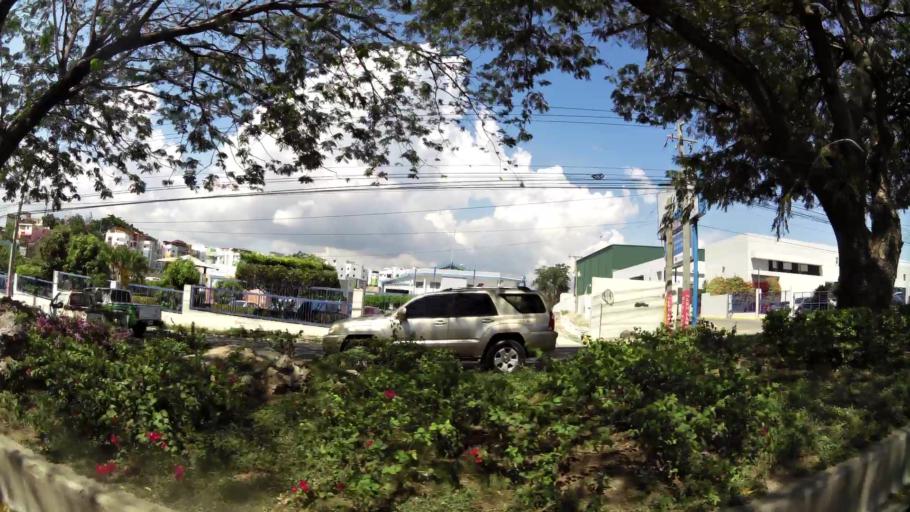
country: DO
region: Nacional
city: Santo Domingo
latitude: 18.4599
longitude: -69.9879
